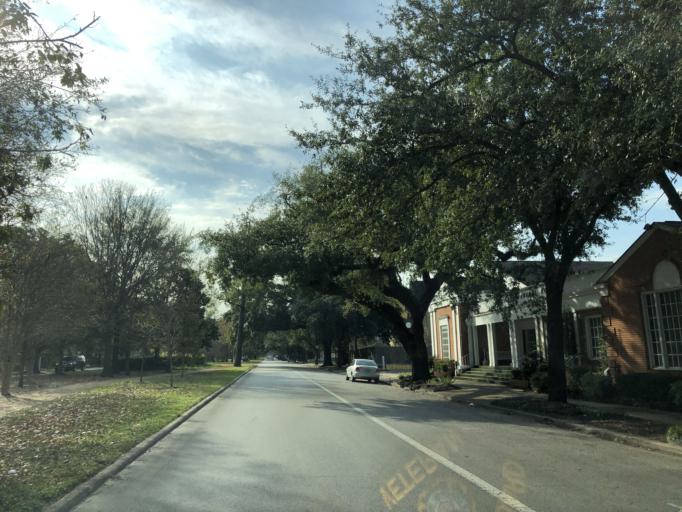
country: US
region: Texas
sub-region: Harris County
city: Houston
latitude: 29.7952
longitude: -95.3978
